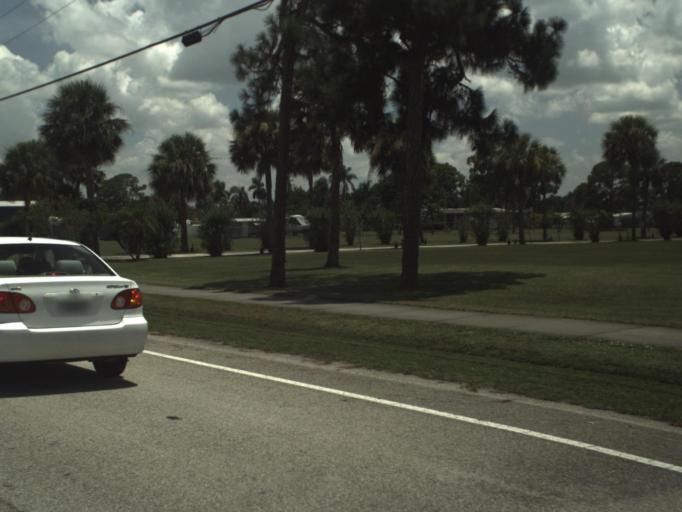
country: US
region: Florida
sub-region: Martin County
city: Port Salerno
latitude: 27.1469
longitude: -80.2154
